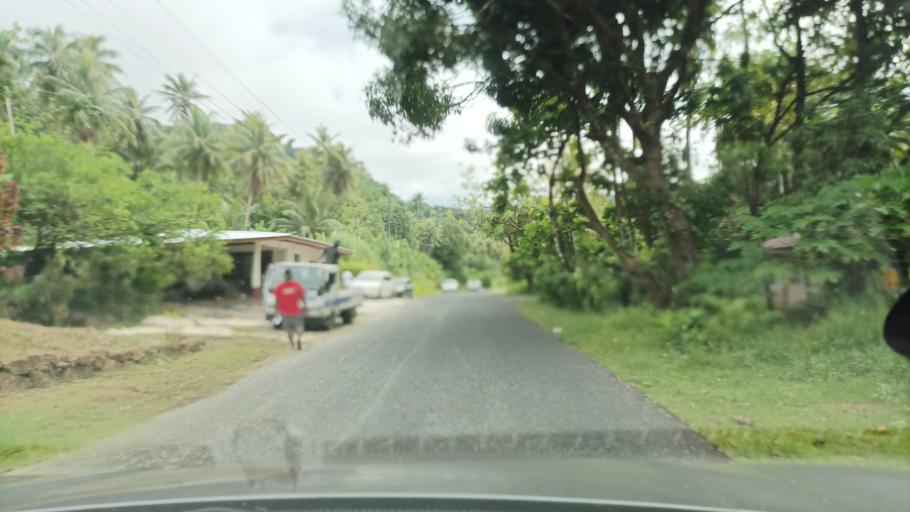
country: FM
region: Pohnpei
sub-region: Kolonia Municipality
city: Kolonia
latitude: 6.9605
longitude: 158.2731
